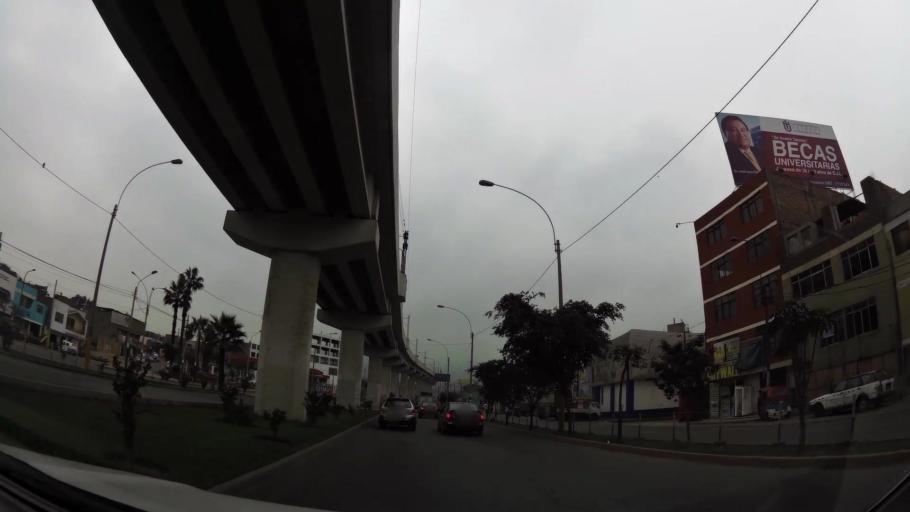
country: PE
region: Lima
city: Lima
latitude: -12.0208
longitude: -77.0054
